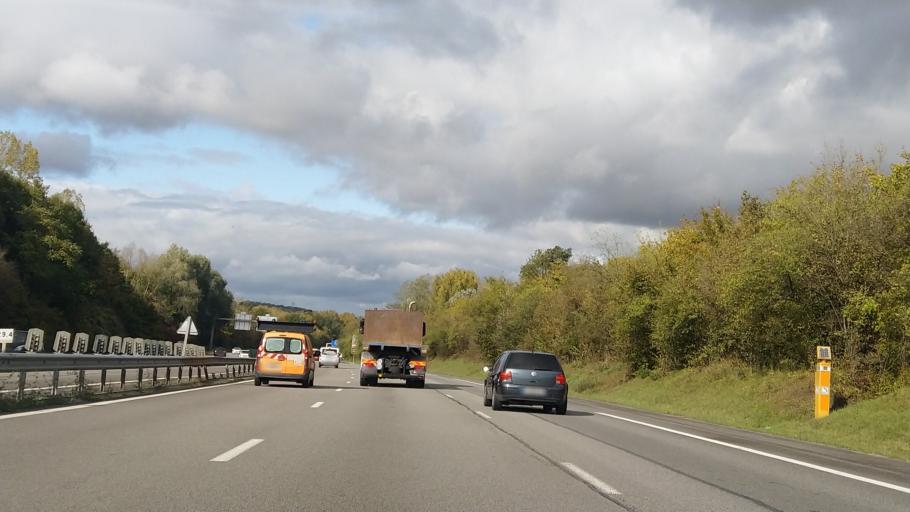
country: FR
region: Ile-de-France
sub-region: Departement du Val-d'Oise
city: Mours
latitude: 49.1112
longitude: 2.2557
